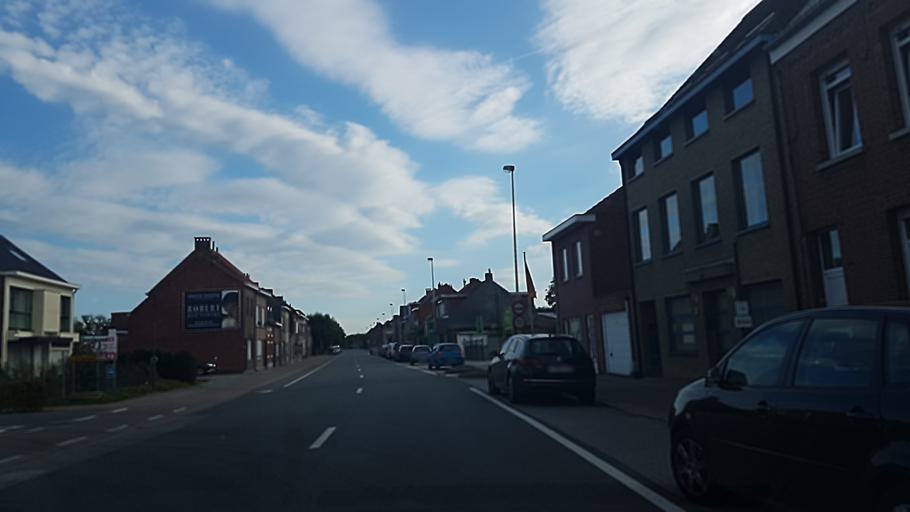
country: BE
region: Flanders
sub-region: Provincie Antwerpen
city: Stabroek
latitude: 51.3412
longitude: 4.4036
